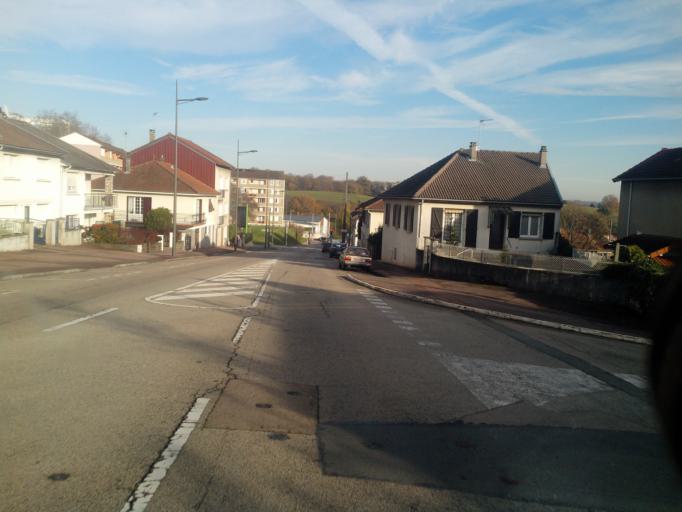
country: FR
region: Limousin
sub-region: Departement de la Haute-Vienne
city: Limoges
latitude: 45.8514
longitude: 1.2699
